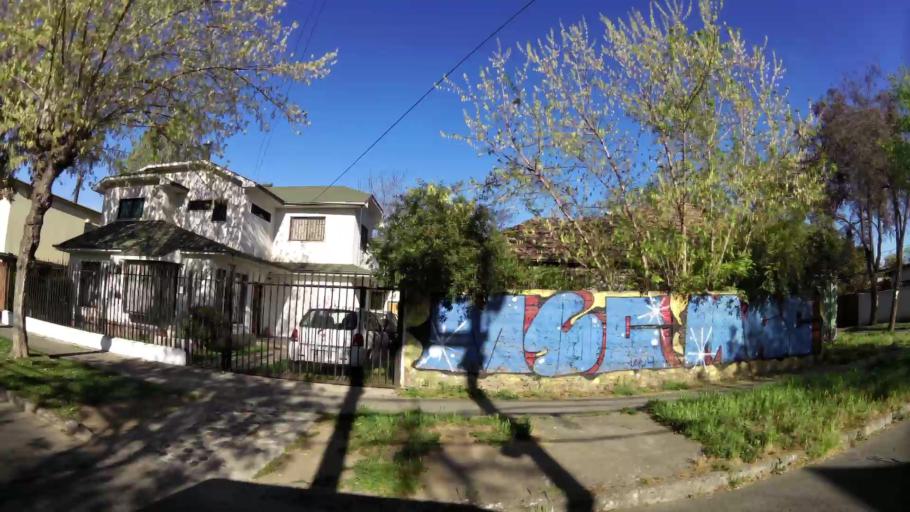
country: CL
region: Santiago Metropolitan
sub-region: Provincia de Santiago
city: Villa Presidente Frei, Nunoa, Santiago, Chile
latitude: -33.4539
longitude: -70.5601
